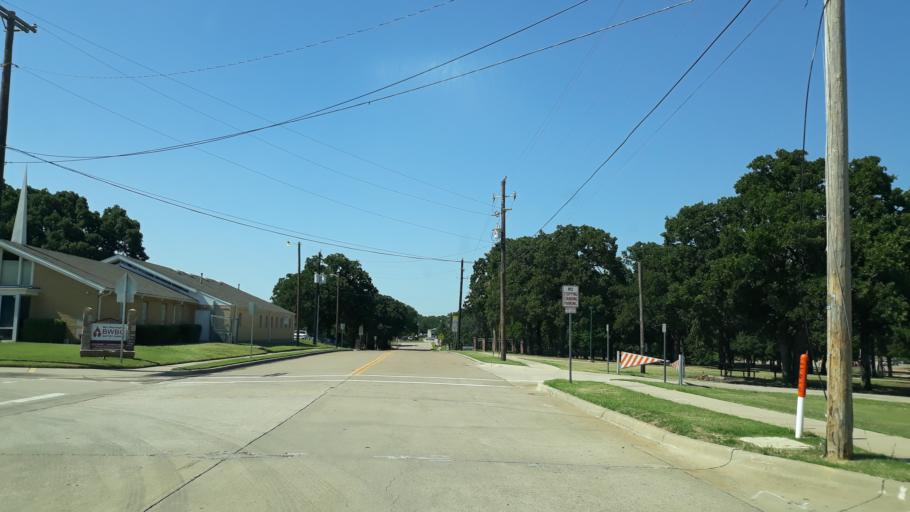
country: US
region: Texas
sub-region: Dallas County
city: Irving
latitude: 32.8190
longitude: -97.0002
